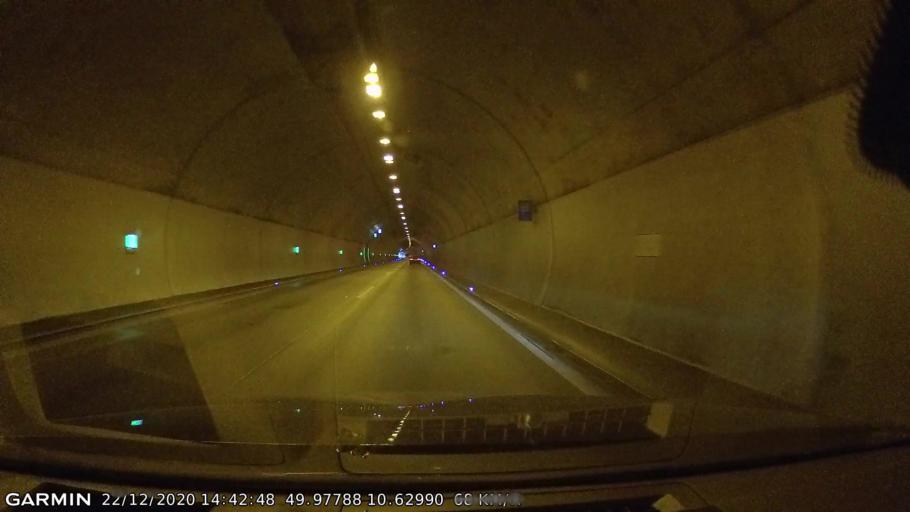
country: DE
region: Bavaria
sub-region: Regierungsbezirk Unterfranken
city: Eltmann
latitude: 49.9779
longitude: 10.6300
